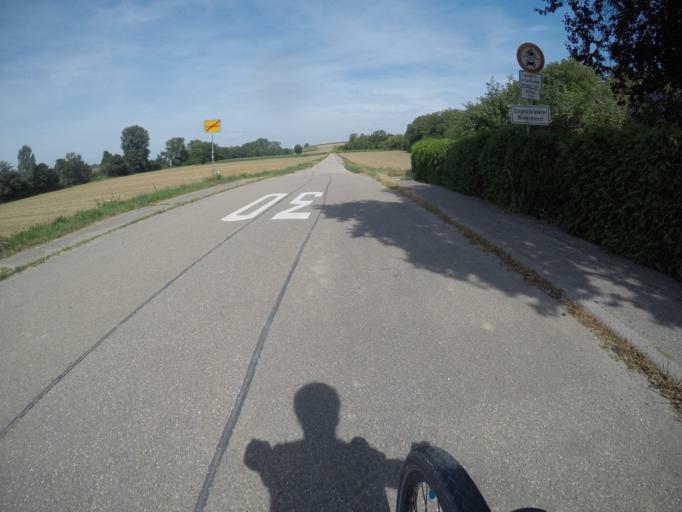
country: DE
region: Baden-Wuerttemberg
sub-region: Karlsruhe Region
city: Gondelsheim
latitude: 49.0457
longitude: 8.6749
